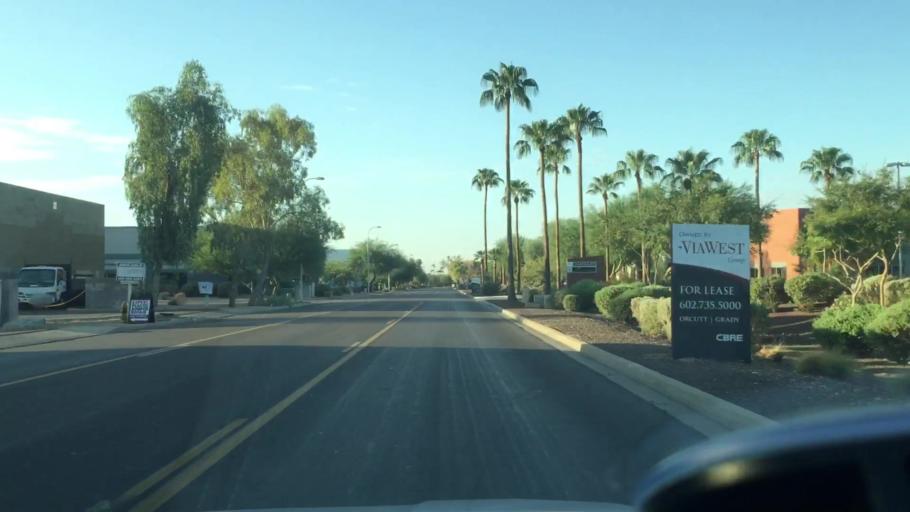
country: US
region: Arizona
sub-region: Maricopa County
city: Guadalupe
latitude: 33.3115
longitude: -111.9674
